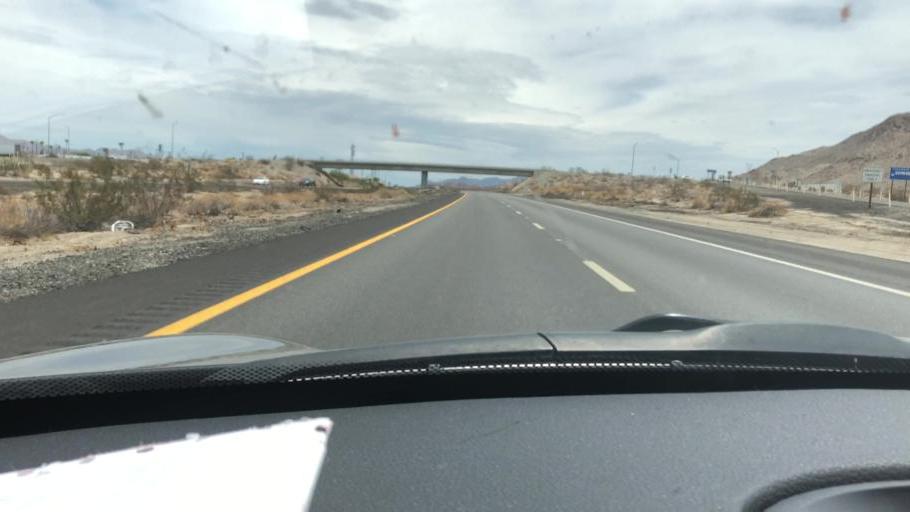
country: US
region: California
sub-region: Riverside County
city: Mecca
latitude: 33.6598
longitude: -115.7268
